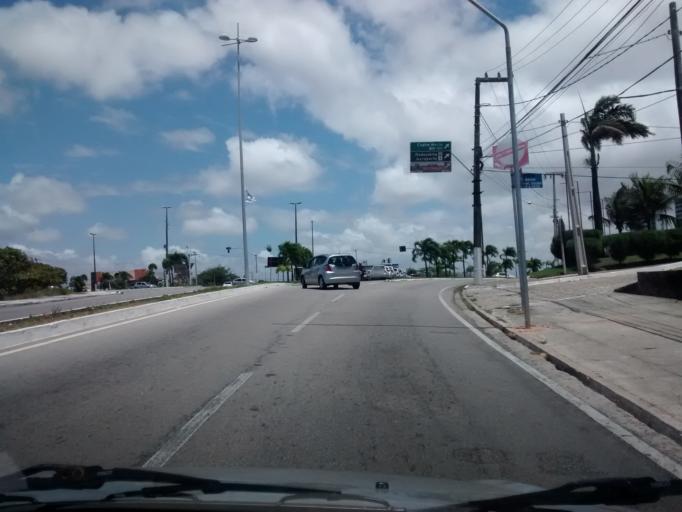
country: BR
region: Rio Grande do Norte
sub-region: Natal
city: Natal
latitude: -5.8666
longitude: -35.1819
